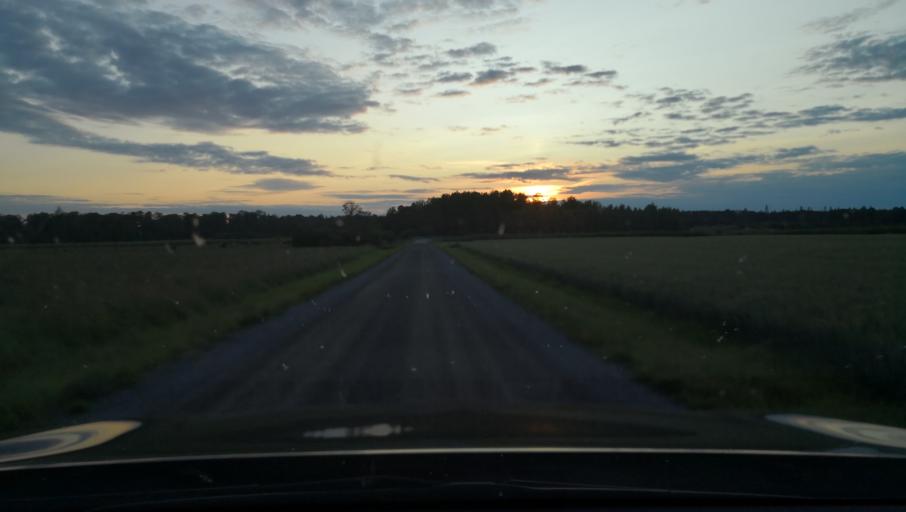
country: SE
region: Uppsala
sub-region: Osthammars Kommun
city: Bjorklinge
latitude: 60.0593
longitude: 17.5851
